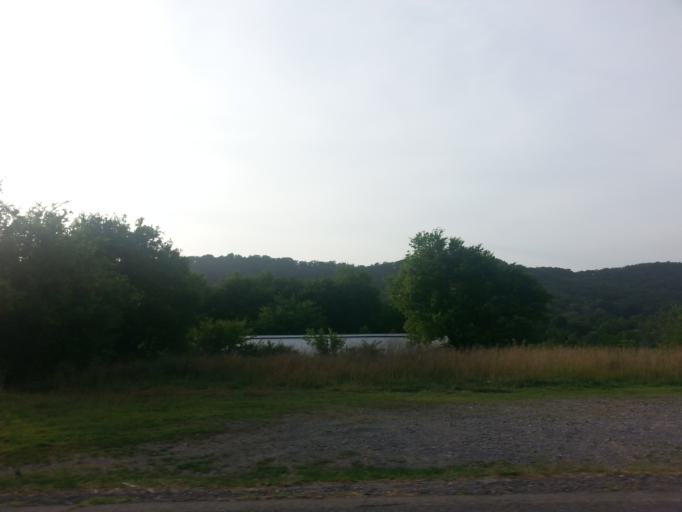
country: US
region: Tennessee
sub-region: Blount County
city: Wildwood
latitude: 35.8406
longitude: -83.8382
